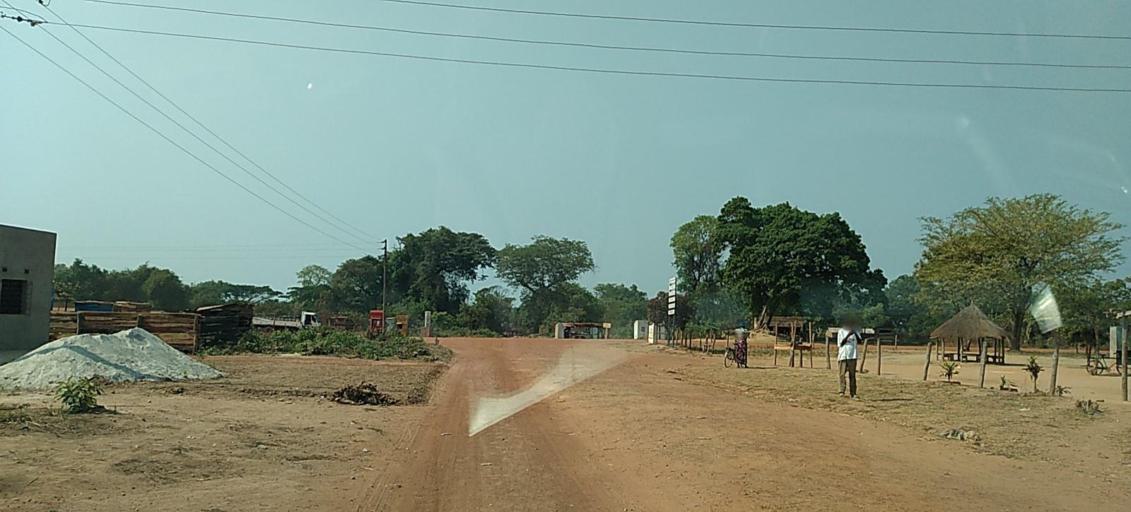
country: ZM
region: Copperbelt
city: Chingola
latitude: -12.9212
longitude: 27.3732
